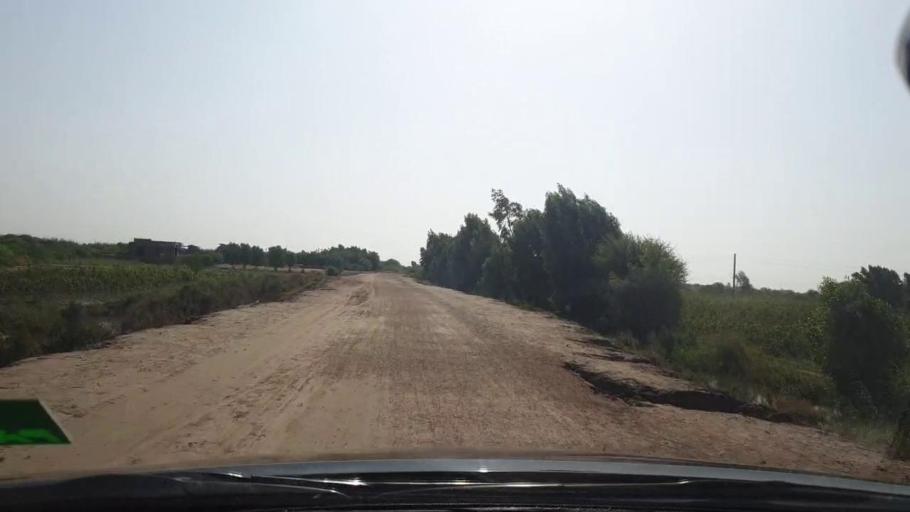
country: PK
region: Sindh
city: Tando Bago
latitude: 24.6976
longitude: 69.0162
